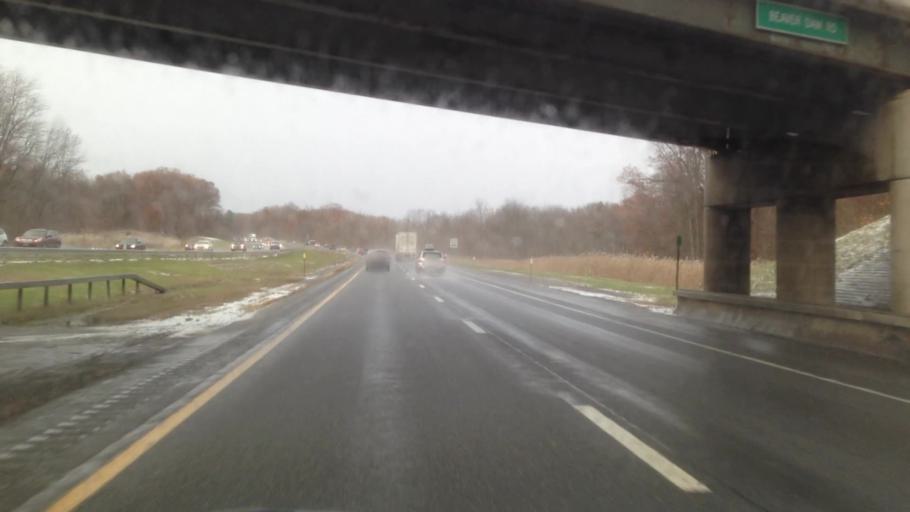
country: US
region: New York
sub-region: Rensselaer County
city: Castleton-on-Hudson
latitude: 42.5412
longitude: -73.7824
